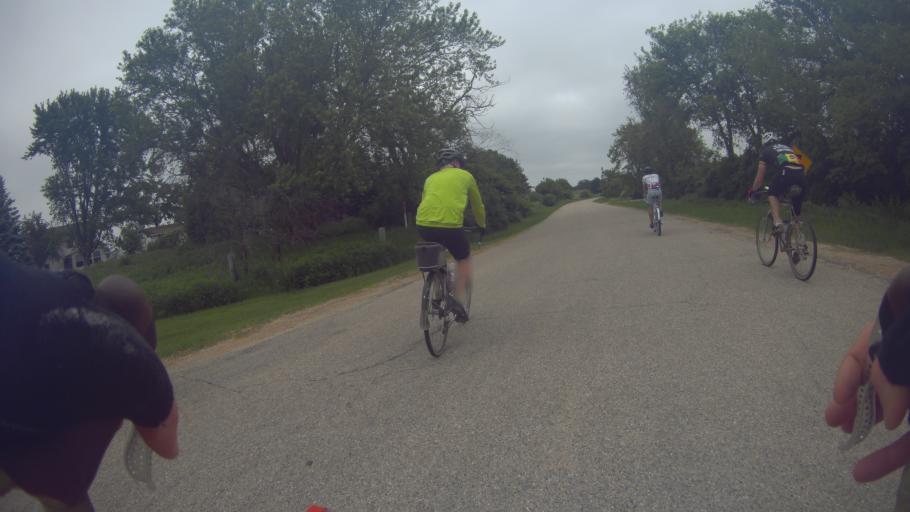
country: US
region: Wisconsin
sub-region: Dane County
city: Oregon
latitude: 42.8891
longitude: -89.3866
